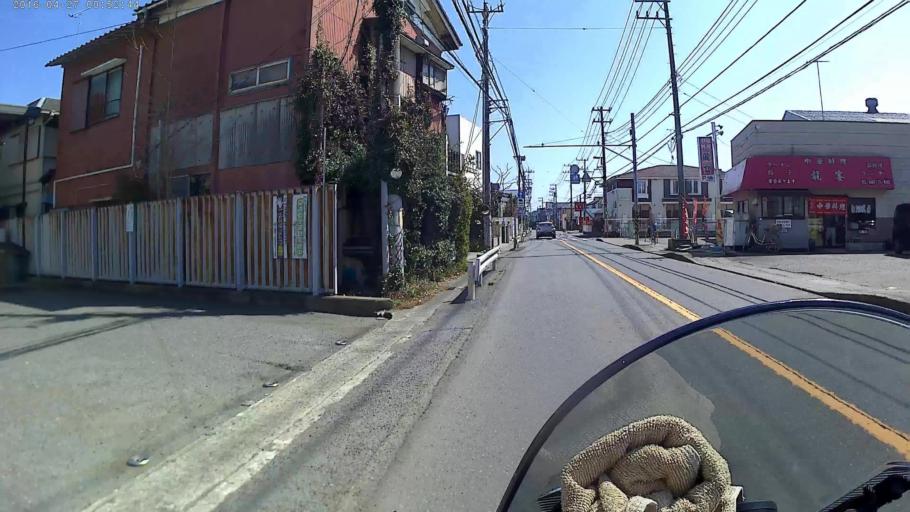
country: JP
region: Kanagawa
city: Chigasaki
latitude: 35.3609
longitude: 139.3899
